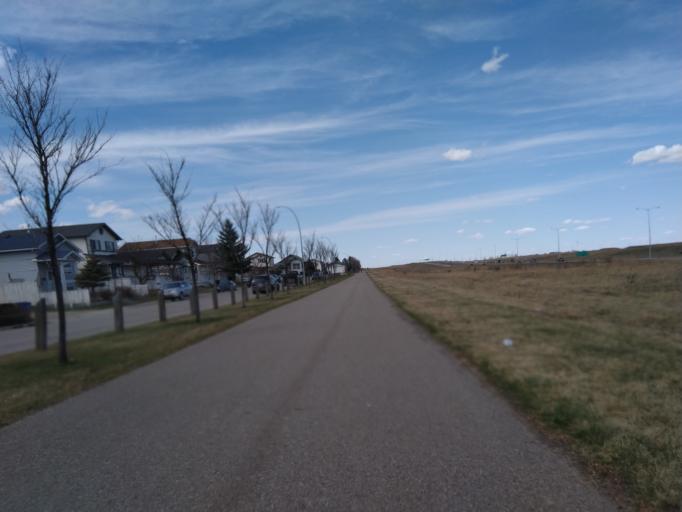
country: CA
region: Alberta
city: Chestermere
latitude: 51.0433
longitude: -113.9229
